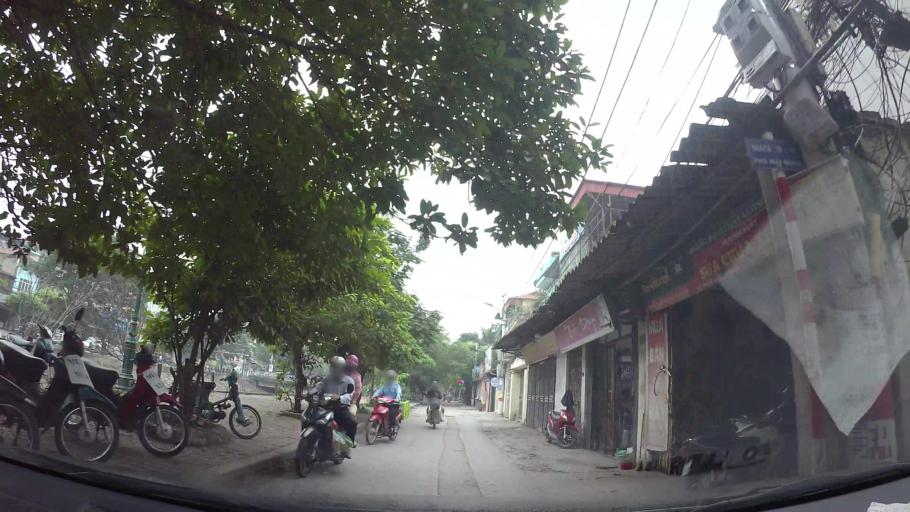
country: VN
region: Ha Noi
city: Hai BaTrung
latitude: 20.9889
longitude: 105.8628
